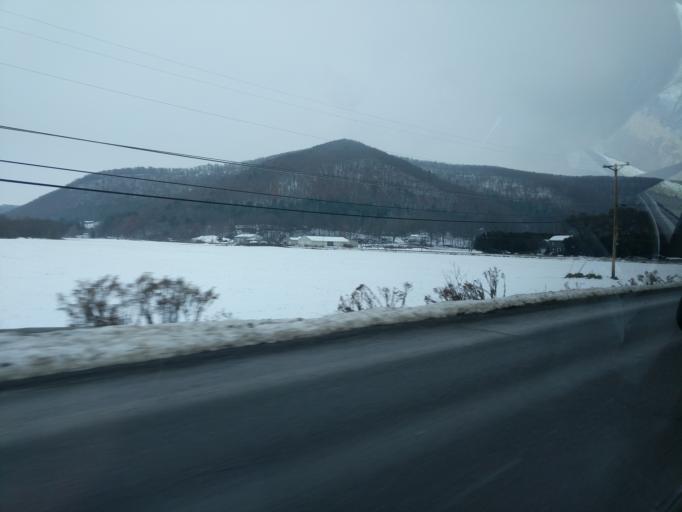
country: US
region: Pennsylvania
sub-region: Tioga County
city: Wellsboro
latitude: 41.8427
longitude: -77.2762
